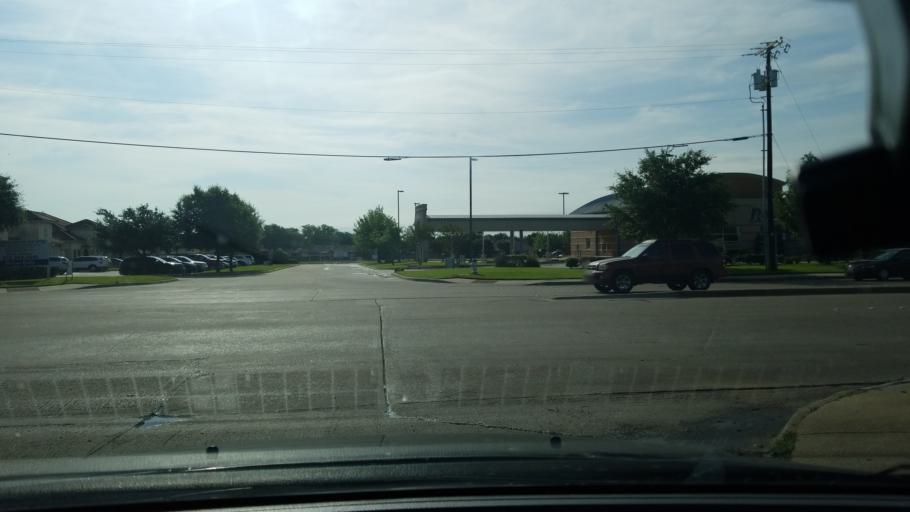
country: US
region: Texas
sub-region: Dallas County
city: Mesquite
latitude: 32.8027
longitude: -96.6114
